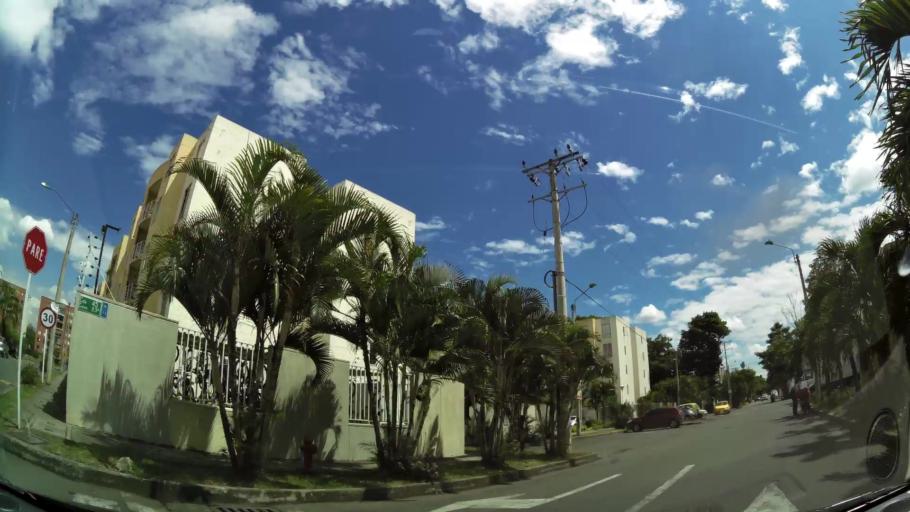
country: CO
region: Valle del Cauca
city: Cali
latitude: 3.3829
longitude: -76.5184
